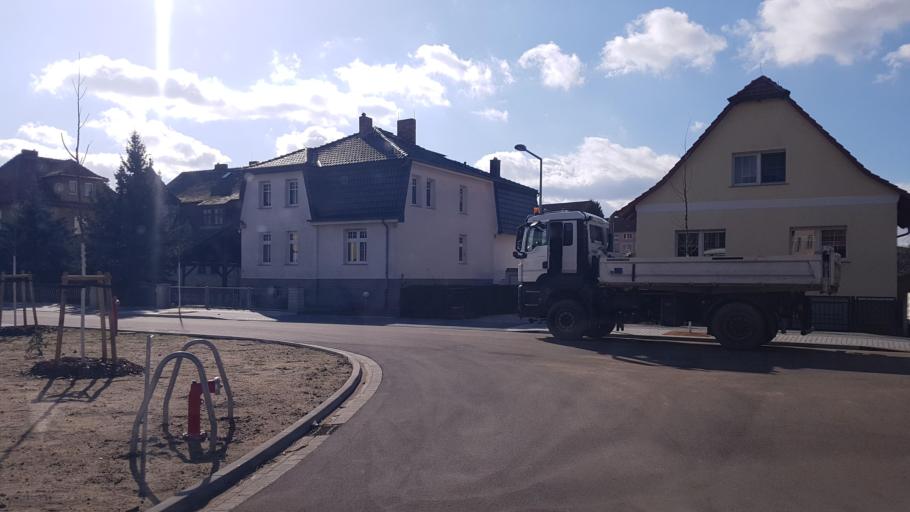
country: DE
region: Brandenburg
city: Herzberg
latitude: 51.6962
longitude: 13.2303
